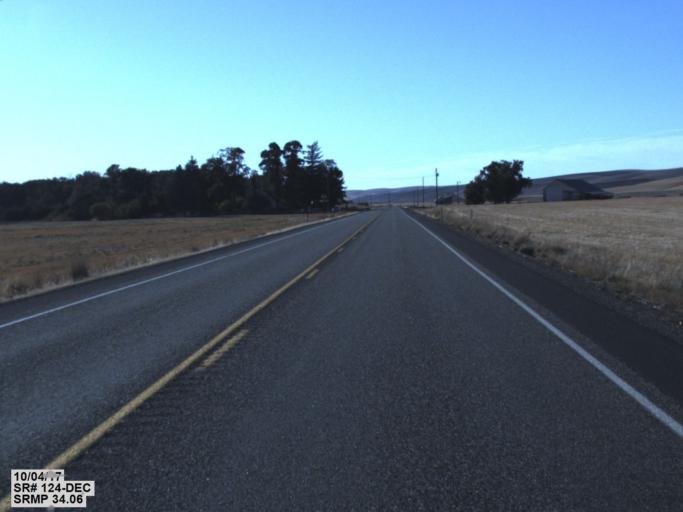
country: US
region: Washington
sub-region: Walla Walla County
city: Waitsburg
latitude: 46.3000
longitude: -118.3574
